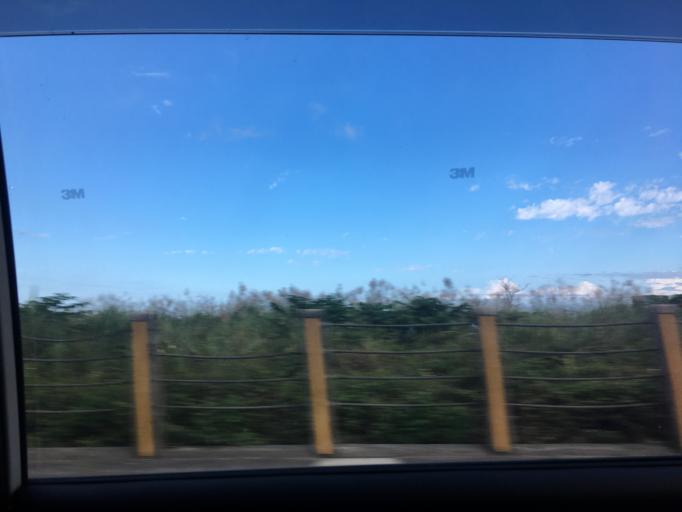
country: TW
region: Taiwan
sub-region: Yilan
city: Yilan
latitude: 24.9205
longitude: 121.8838
